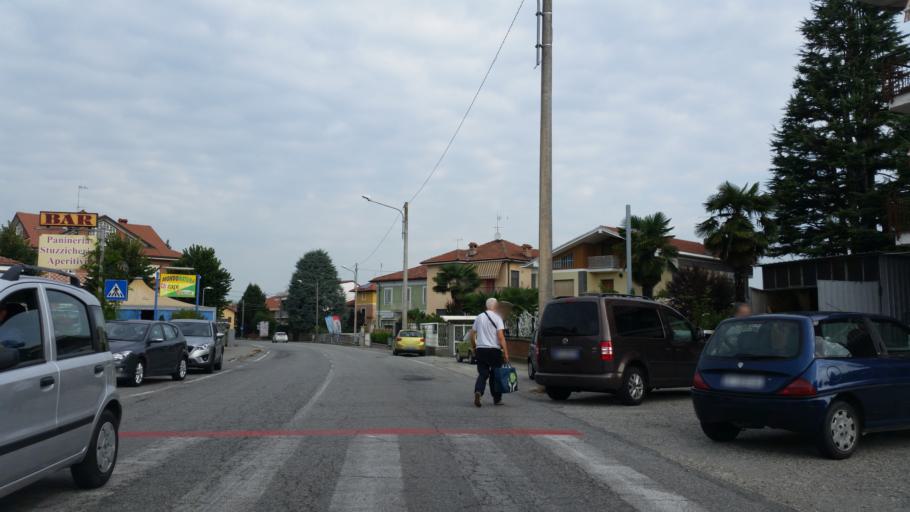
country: IT
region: Piedmont
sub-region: Provincia di Torino
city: Cavagnolo
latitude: 45.1546
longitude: 8.0500
